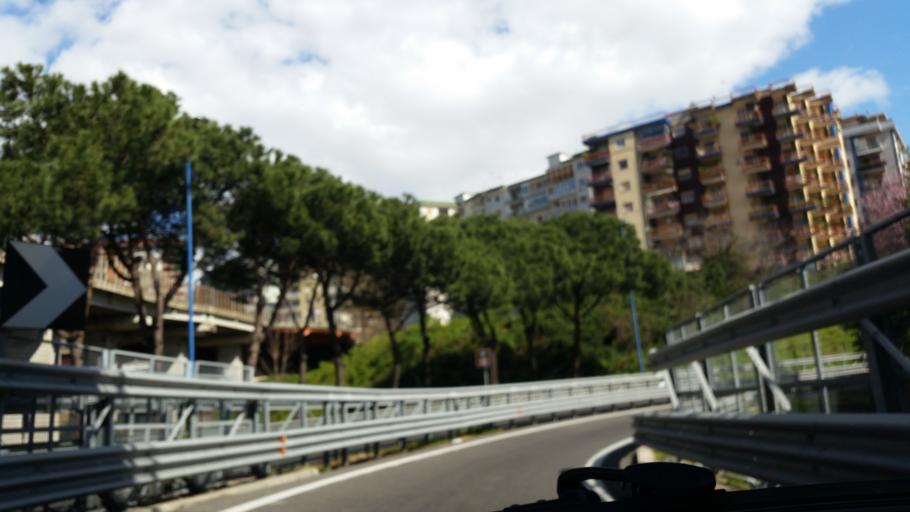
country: IT
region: Campania
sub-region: Provincia di Napoli
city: Napoli
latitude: 40.8456
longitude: 14.2183
